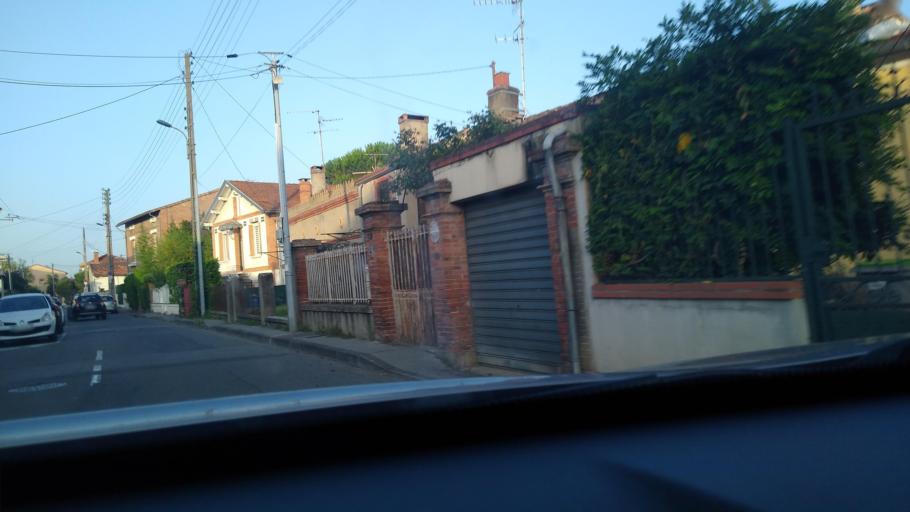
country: FR
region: Midi-Pyrenees
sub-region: Departement de la Haute-Garonne
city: Toulouse
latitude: 43.6297
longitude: 1.4586
